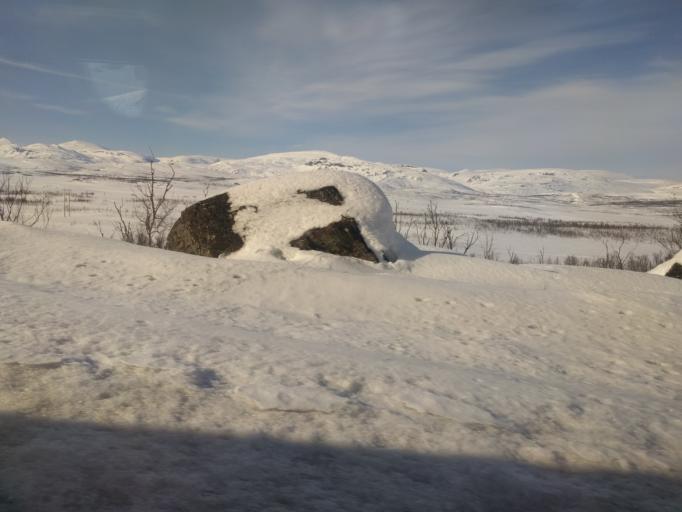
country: NO
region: Troms
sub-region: Bardu
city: Setermoen
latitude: 68.4251
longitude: 18.3851
